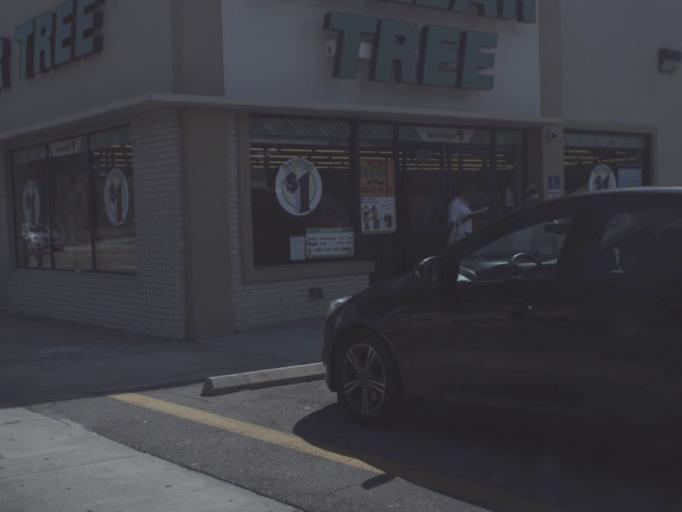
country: US
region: Florida
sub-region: Hillsborough County
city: Tampa
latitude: 27.9926
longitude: -82.4595
